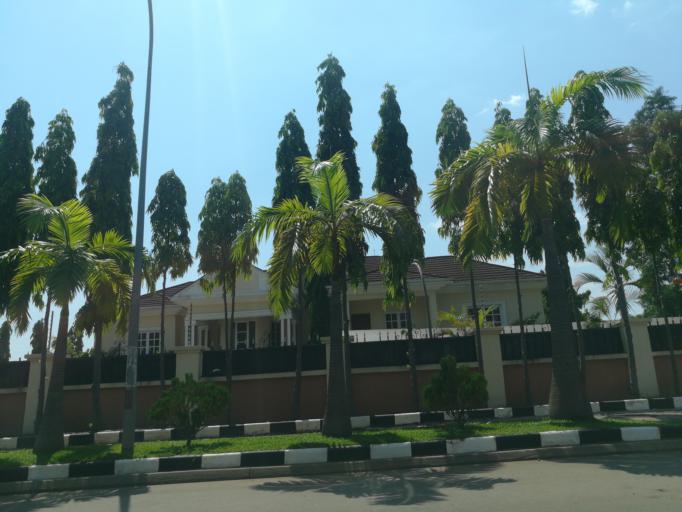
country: NG
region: Abuja Federal Capital Territory
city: Abuja
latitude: 9.0630
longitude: 7.4385
